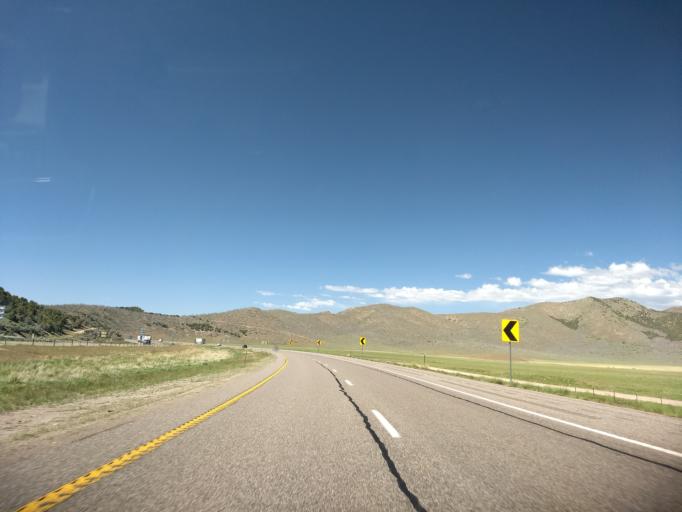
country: US
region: Utah
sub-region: Beaver County
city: Beaver
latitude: 38.6665
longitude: -112.5888
